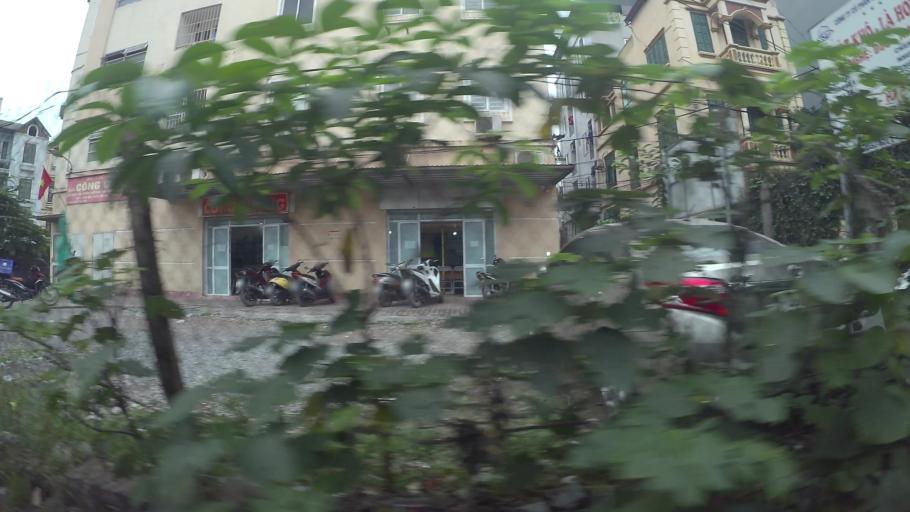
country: VN
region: Ha Noi
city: Hai BaTrung
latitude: 20.9898
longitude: 105.8626
